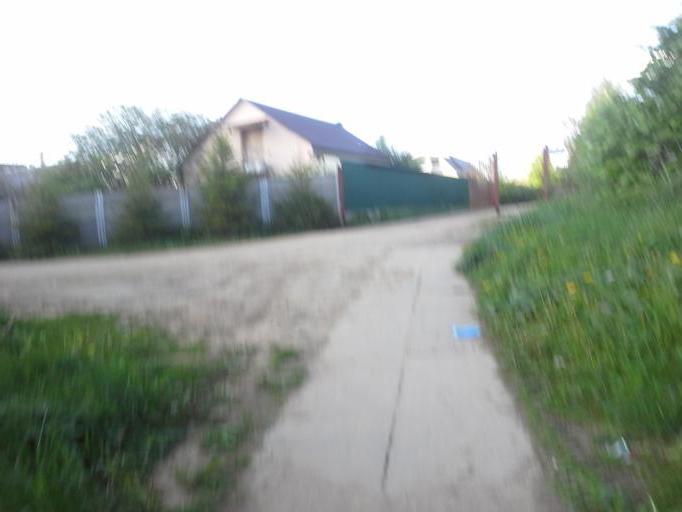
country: RU
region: Moskovskaya
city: Zhavoronki
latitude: 55.6701
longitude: 37.1449
